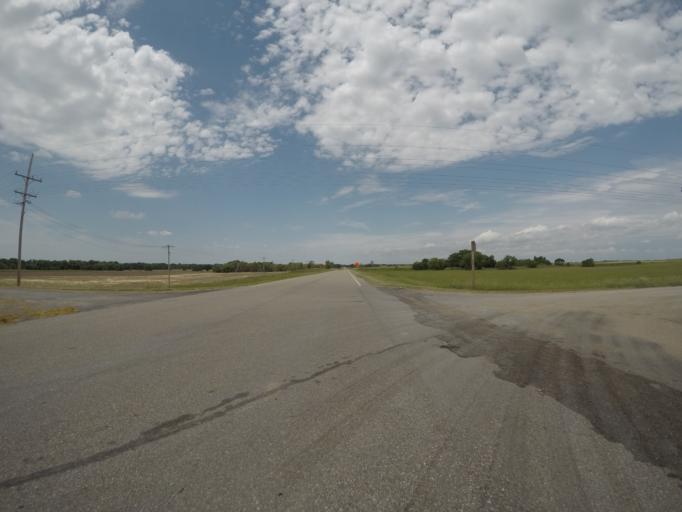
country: US
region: Kansas
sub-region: Graham County
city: Hill City
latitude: 39.3944
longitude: -99.6210
